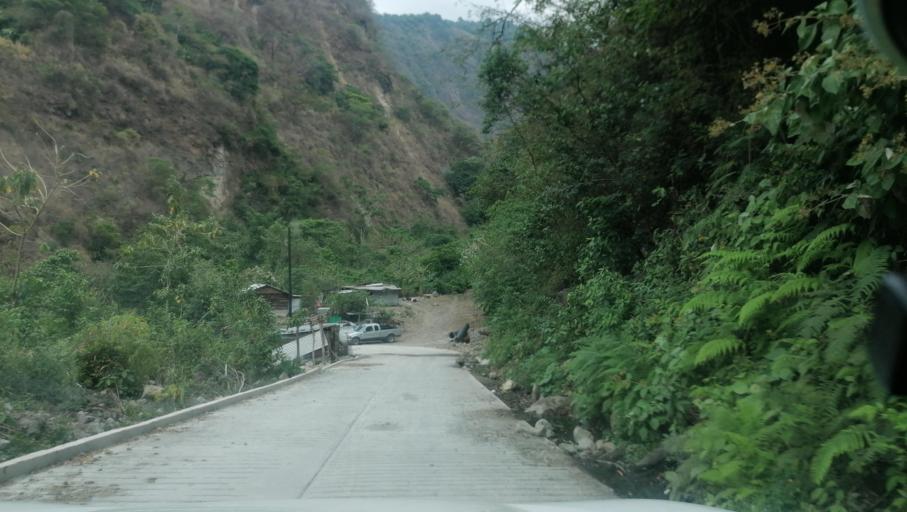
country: MX
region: Chiapas
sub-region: Cacahoatan
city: Benito Juarez
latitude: 15.1672
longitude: -92.1780
